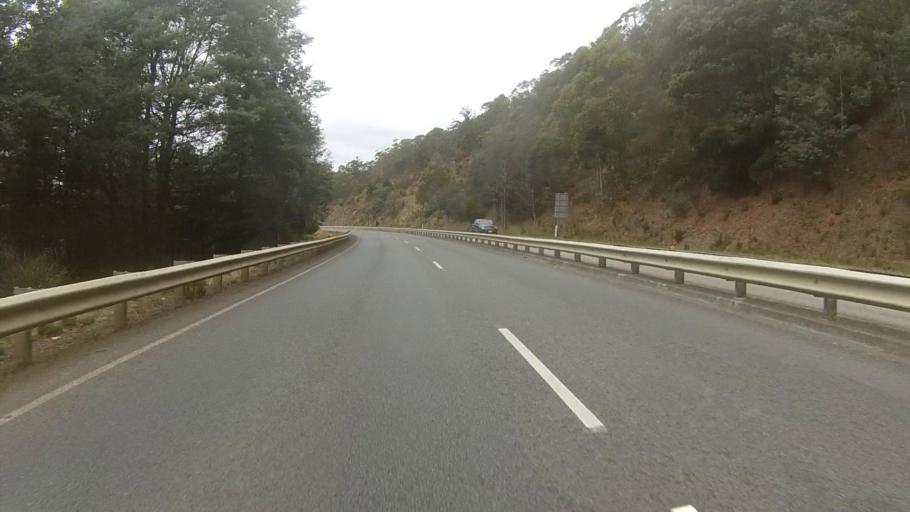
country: AU
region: Tasmania
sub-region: Kingborough
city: Margate
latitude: -42.9834
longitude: 147.1786
